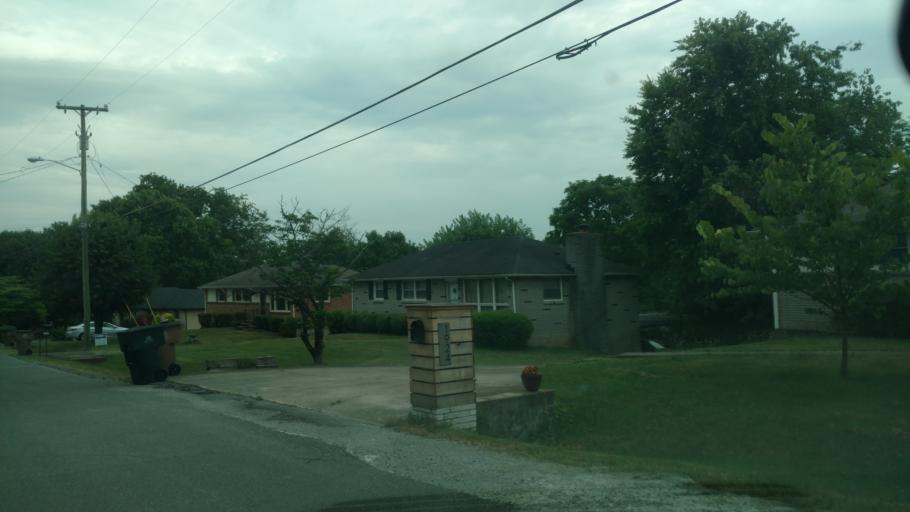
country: US
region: Tennessee
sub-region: Davidson County
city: Nashville
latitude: 36.1967
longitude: -86.7110
